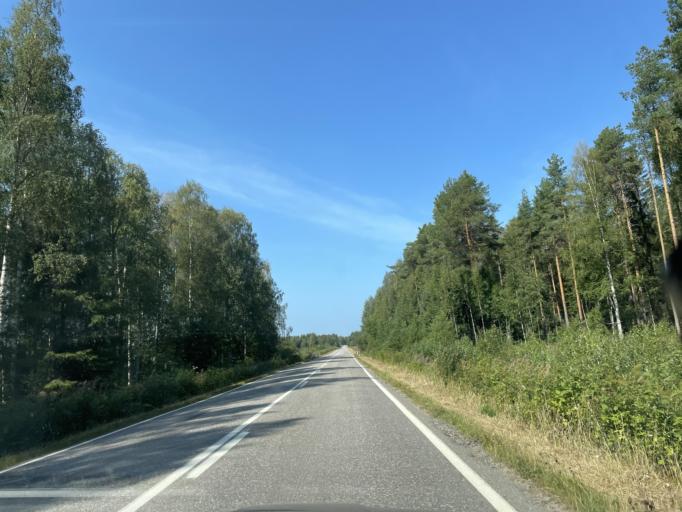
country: FI
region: Central Finland
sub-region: Saarijaervi-Viitasaari
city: Pihtipudas
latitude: 63.3639
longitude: 25.6509
